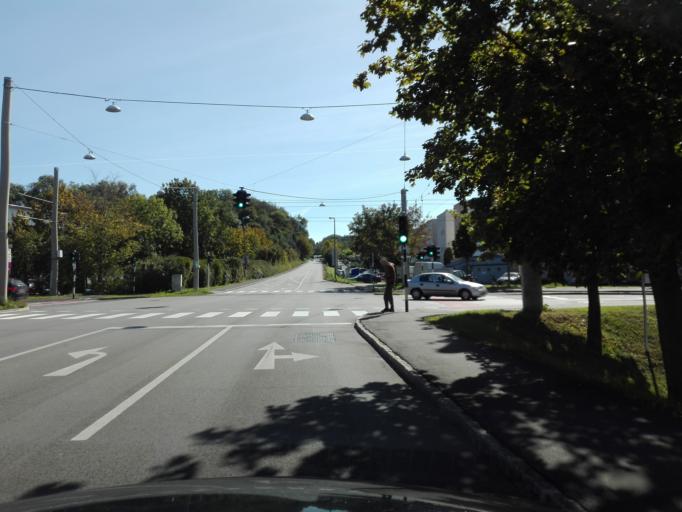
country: AT
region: Upper Austria
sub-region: Politischer Bezirk Linz-Land
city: Ansfelden
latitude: 48.2410
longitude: 14.3346
